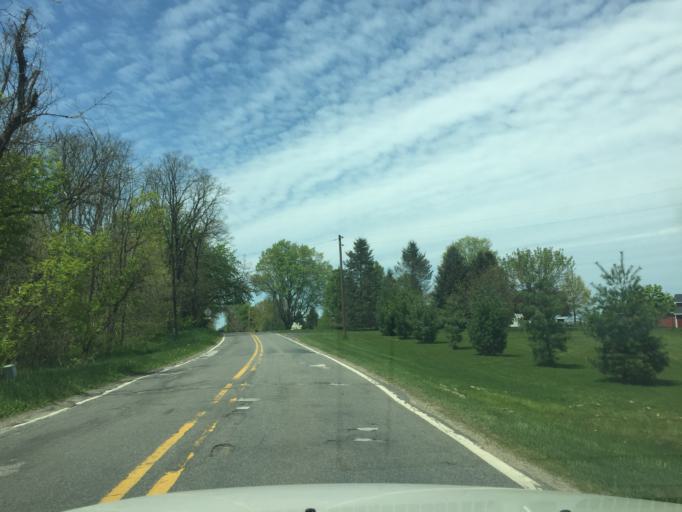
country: US
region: Michigan
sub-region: Berrien County
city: Stevensville
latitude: 41.9450
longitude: -86.4718
